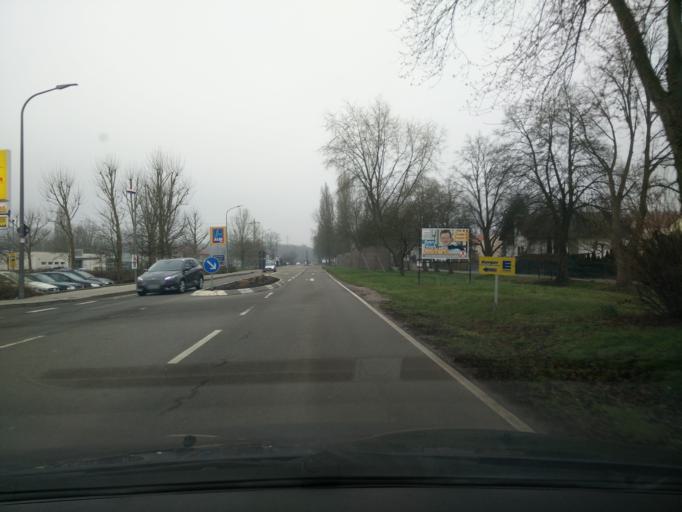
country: DE
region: Rheinland-Pfalz
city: Kandel
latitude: 49.0770
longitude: 8.2012
